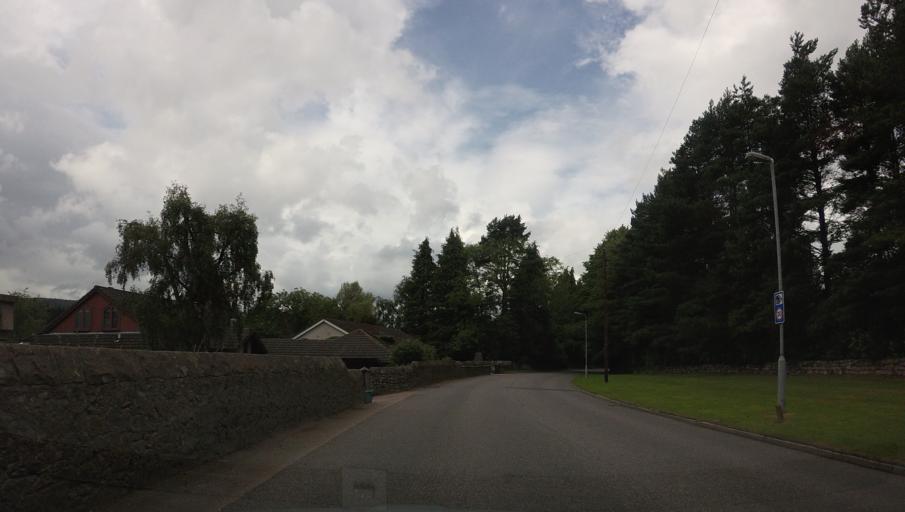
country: GB
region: Scotland
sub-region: Aberdeenshire
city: Banchory
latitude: 57.0543
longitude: -2.5194
